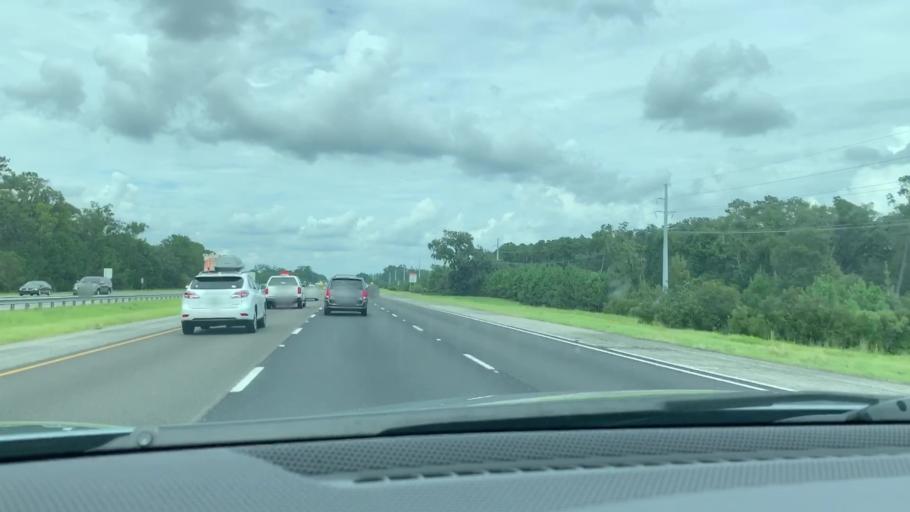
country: US
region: Georgia
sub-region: Liberty County
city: Midway
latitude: 31.8005
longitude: -81.3704
